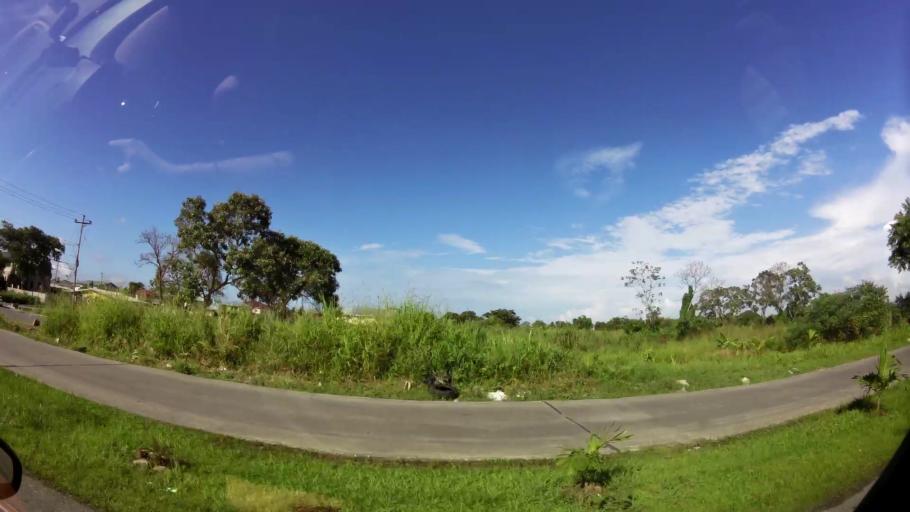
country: TT
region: Chaguanas
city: Chaguanas
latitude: 10.5265
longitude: -61.3962
